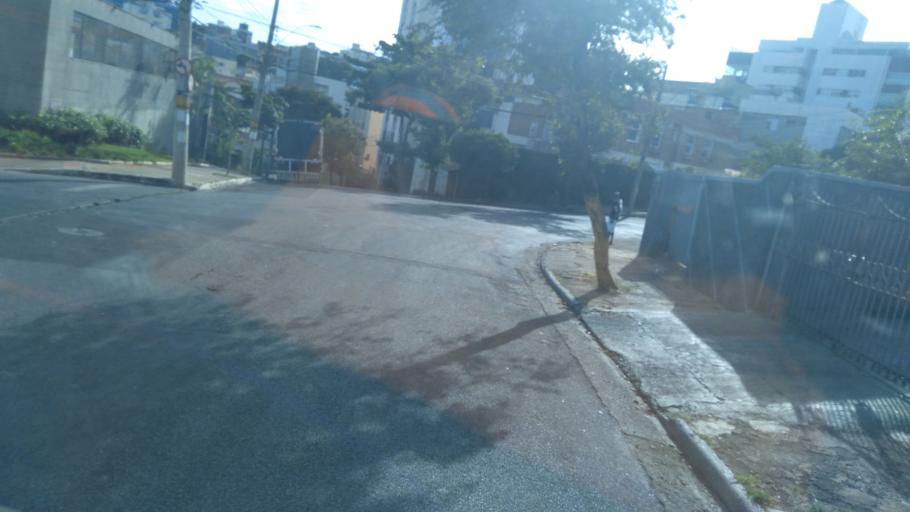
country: BR
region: Minas Gerais
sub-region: Belo Horizonte
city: Belo Horizonte
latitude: -19.8840
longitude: -43.9280
